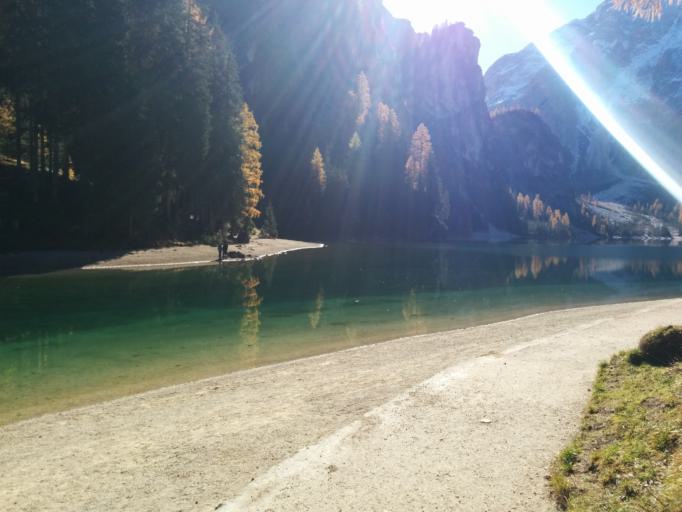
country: IT
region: Trentino-Alto Adige
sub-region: Bolzano
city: Braies
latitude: 46.6990
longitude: 12.0869
